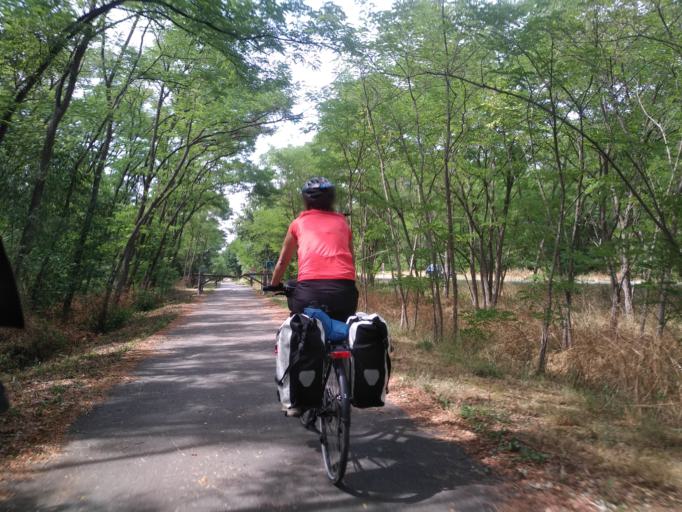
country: FR
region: Auvergne
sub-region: Departement de l'Allier
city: Diou
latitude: 46.5439
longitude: 3.7458
